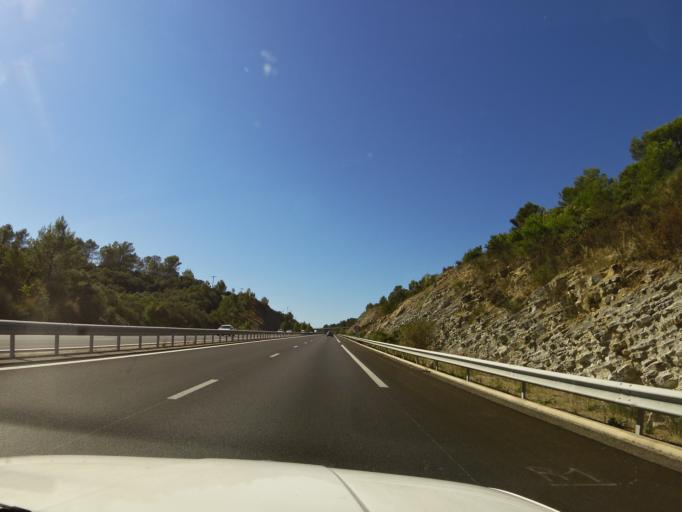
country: FR
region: Languedoc-Roussillon
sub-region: Departement du Gard
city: Vezenobres
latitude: 44.0581
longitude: 4.1230
